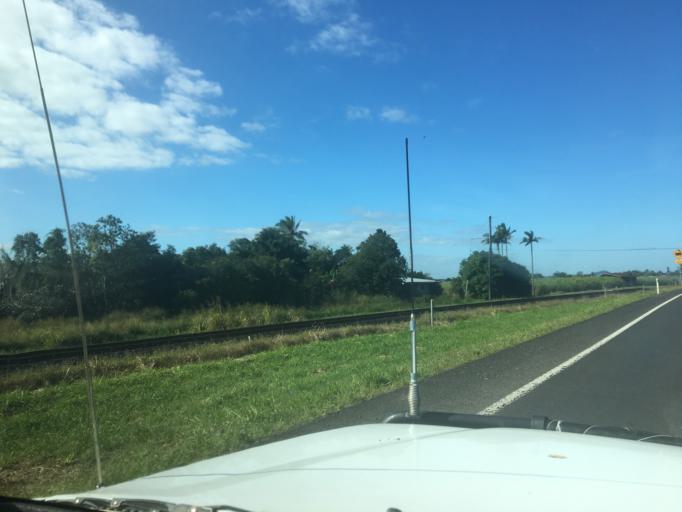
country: AU
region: Queensland
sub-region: Cassowary Coast
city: Innisfail
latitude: -17.3252
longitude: 145.9287
